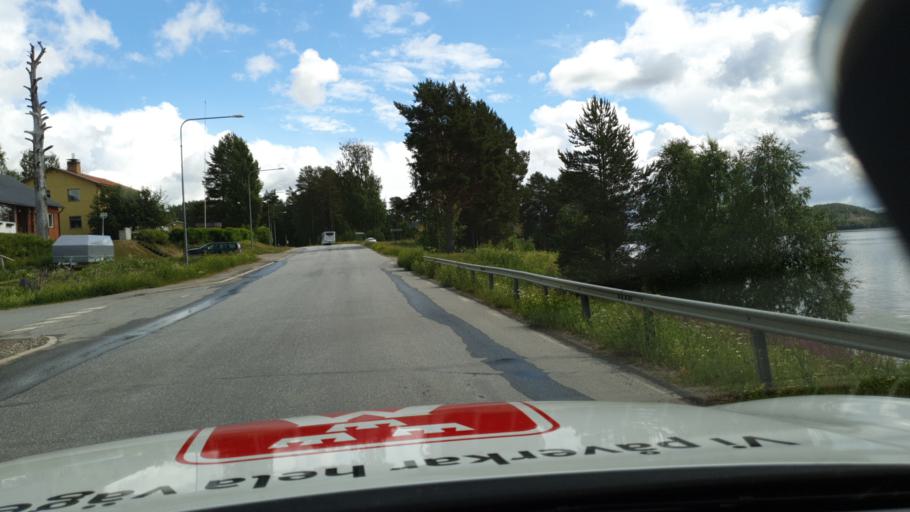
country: SE
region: Vaesterbotten
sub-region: Dorotea Kommun
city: Dorotea
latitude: 64.1198
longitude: 16.2102
